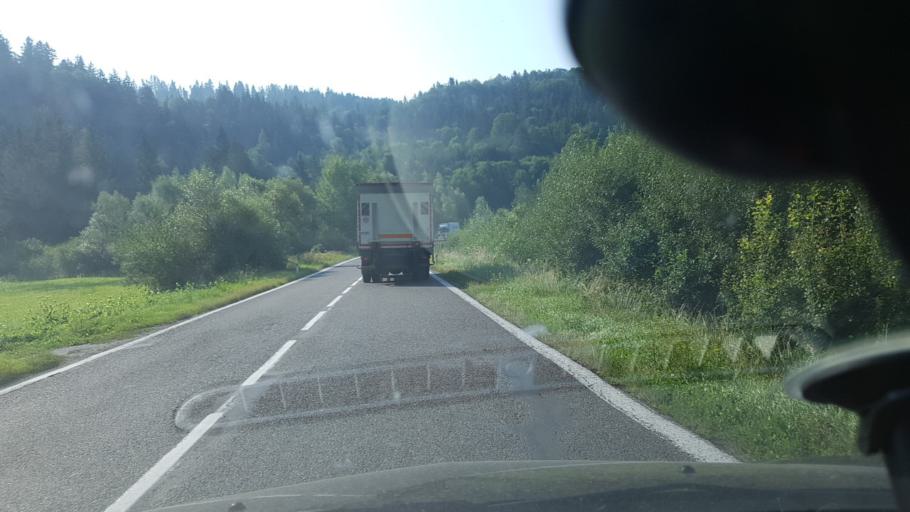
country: SK
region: Zilinsky
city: Tvrdosin
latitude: 49.2913
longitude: 19.4932
